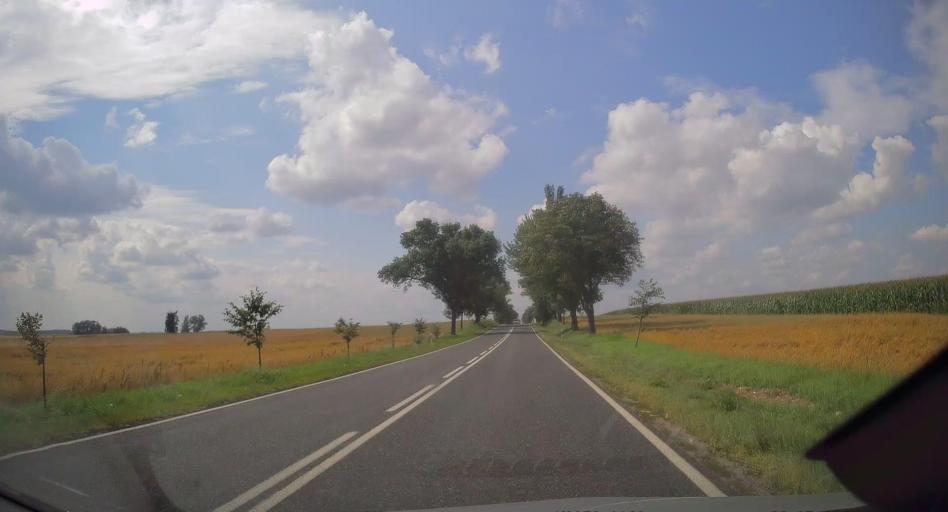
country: PL
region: Lodz Voivodeship
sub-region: Powiat skierniewicki
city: Gluchow
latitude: 51.7926
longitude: 20.0390
